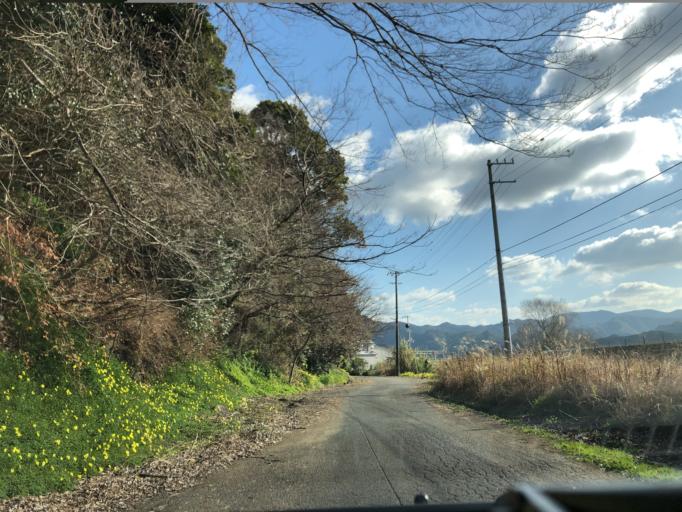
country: JP
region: Kochi
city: Sukumo
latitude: 32.9122
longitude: 132.6998
